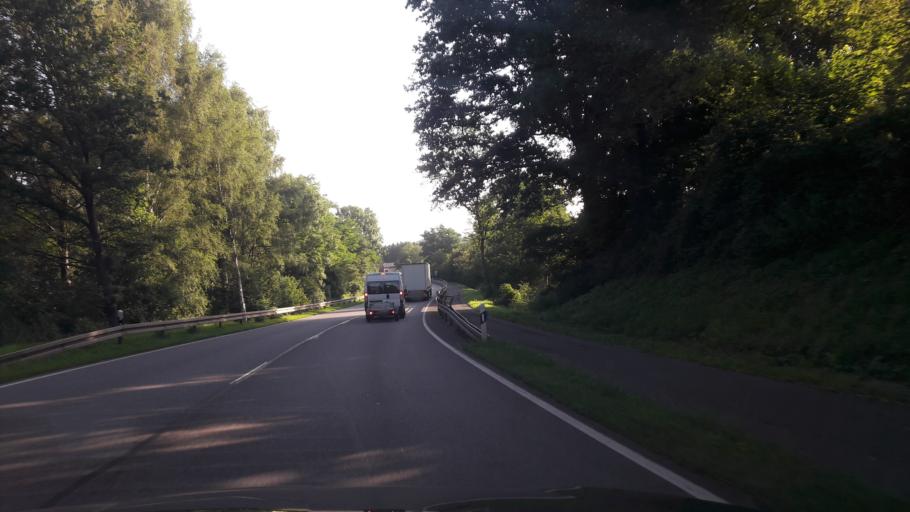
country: DE
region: Saarland
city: Lebach
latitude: 49.3830
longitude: 6.9260
